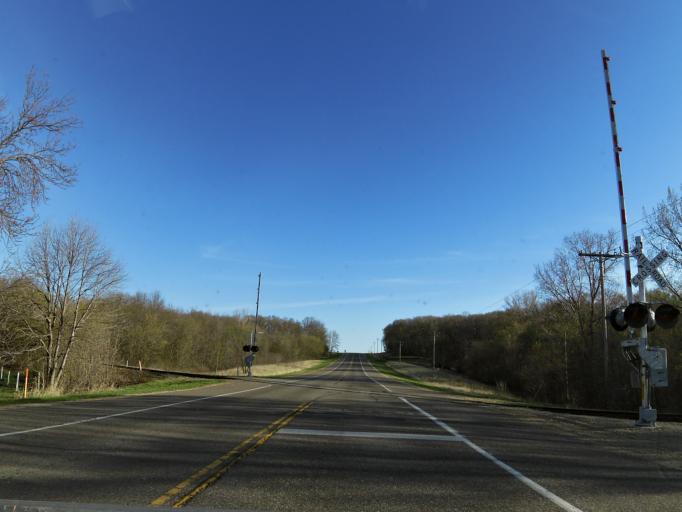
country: US
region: Minnesota
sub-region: Dakota County
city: Lakeville
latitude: 44.5692
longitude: -93.2076
